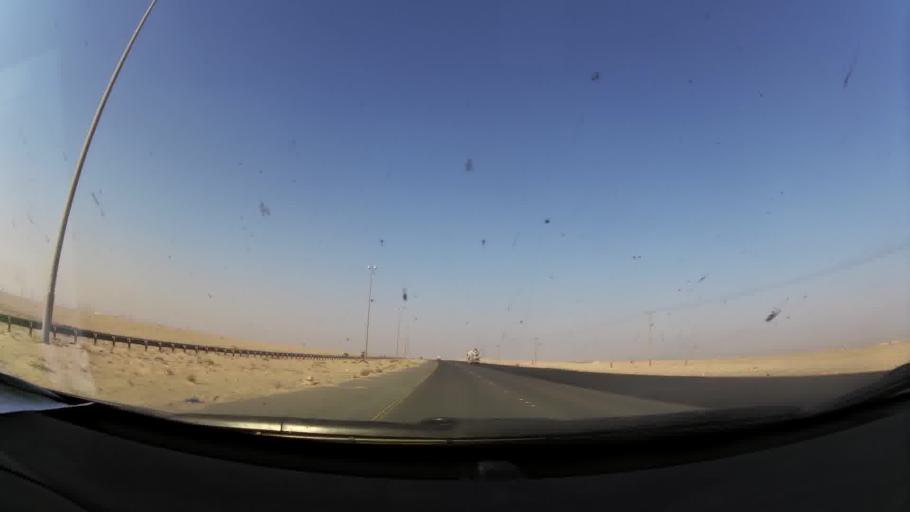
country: KW
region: Muhafazat al Jahra'
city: Al Jahra'
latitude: 29.7080
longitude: 47.6714
